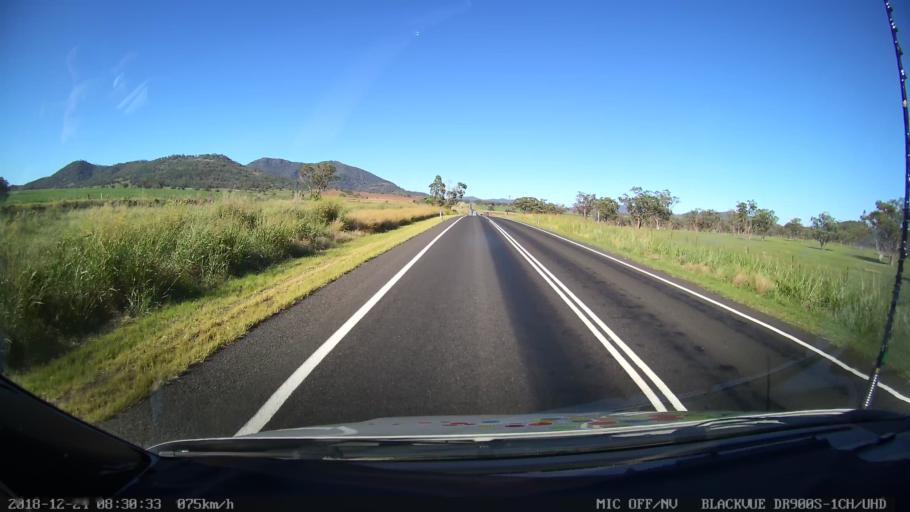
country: AU
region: New South Wales
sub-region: Tamworth Municipality
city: Phillip
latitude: -31.2681
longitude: 150.7232
